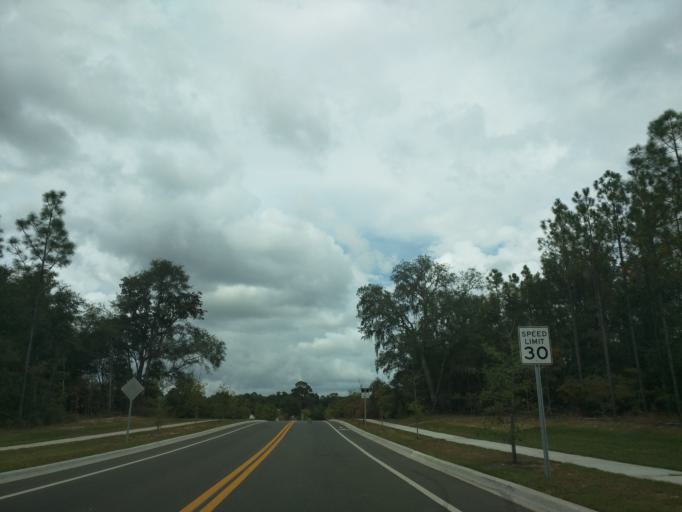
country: US
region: Florida
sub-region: Leon County
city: Woodville
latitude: 30.3828
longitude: -84.2102
